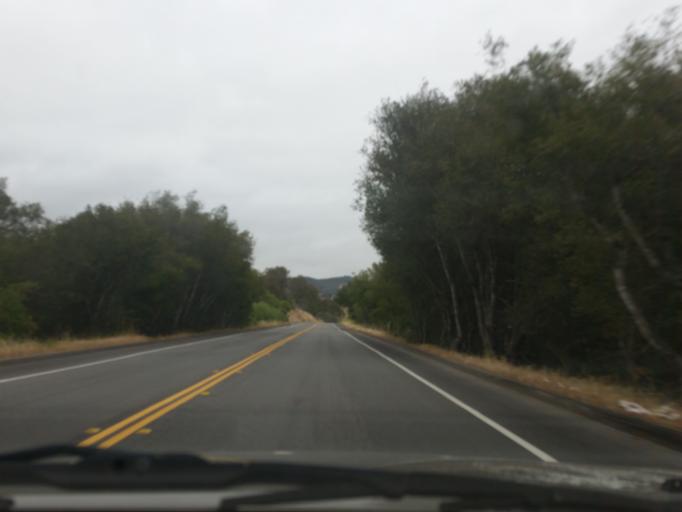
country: US
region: California
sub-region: San Luis Obispo County
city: Avila Beach
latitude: 35.1956
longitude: -120.7064
